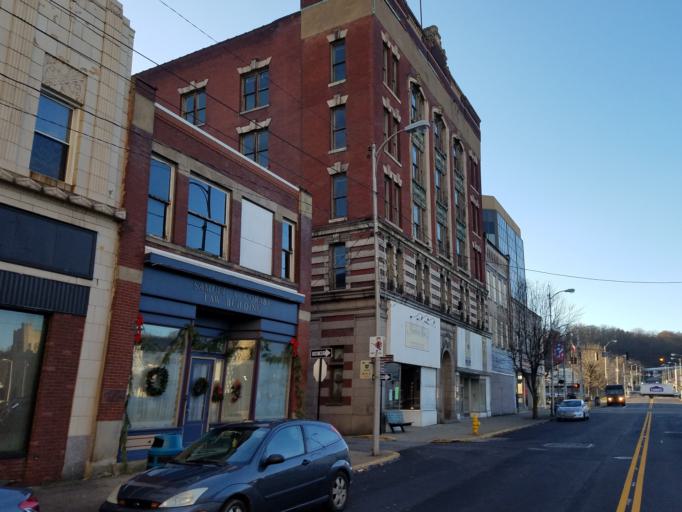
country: US
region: Ohio
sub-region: Jefferson County
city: Steubenville
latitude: 40.3602
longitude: -80.6154
